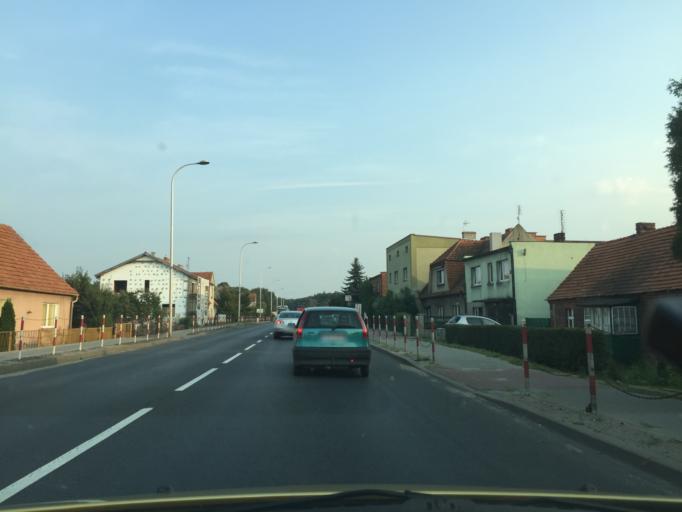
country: PL
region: Greater Poland Voivodeship
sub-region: Powiat jarocinski
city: Jarocin
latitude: 51.9592
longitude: 17.5157
